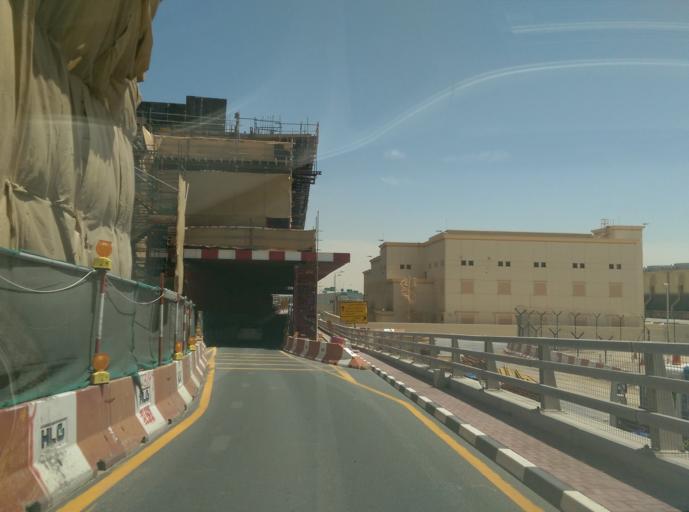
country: AE
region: Dubai
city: Dubai
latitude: 25.0692
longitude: 55.1269
